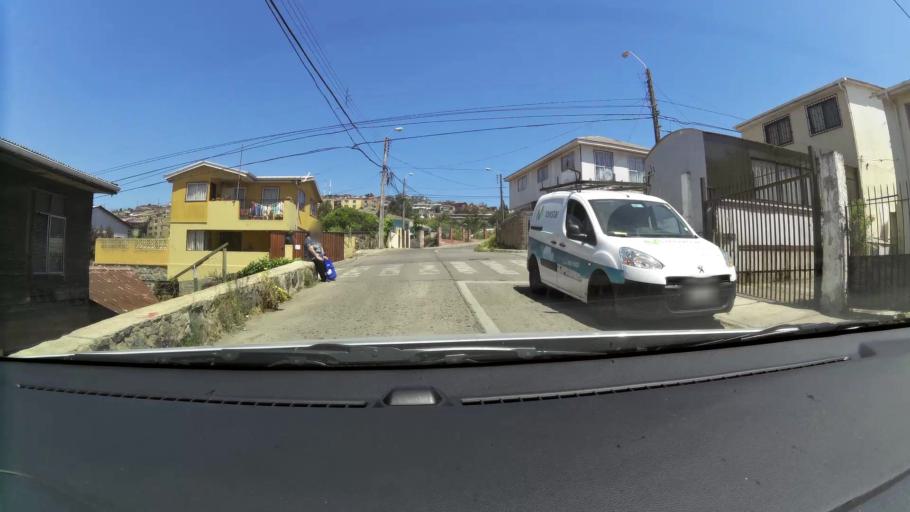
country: CL
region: Valparaiso
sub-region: Provincia de Valparaiso
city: Valparaiso
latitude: -33.0379
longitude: -71.6413
